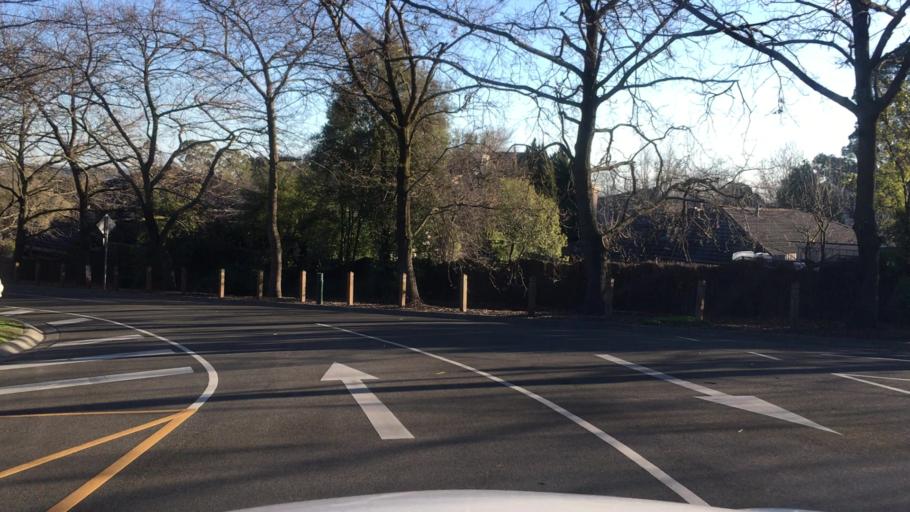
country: AU
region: Victoria
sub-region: Casey
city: Berwick
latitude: -38.0282
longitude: 145.3366
